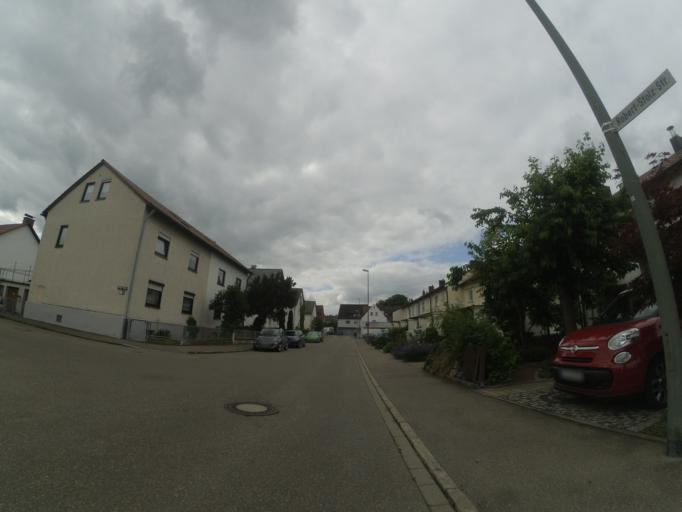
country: DE
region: Bavaria
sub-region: Swabia
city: Neu-Ulm
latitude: 48.4045
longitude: 10.0208
